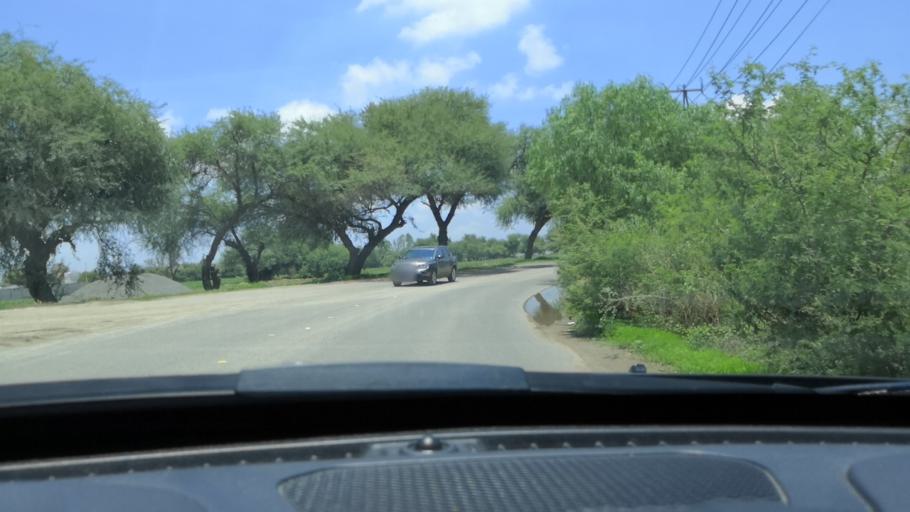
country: MX
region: Guanajuato
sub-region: Leon
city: Ladrilleras del Refugio
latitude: 21.0555
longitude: -101.5598
